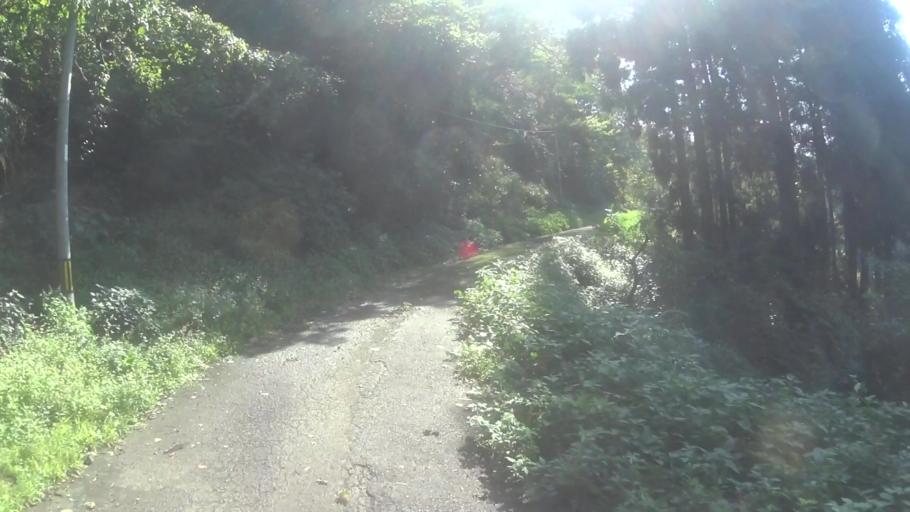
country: JP
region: Kyoto
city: Miyazu
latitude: 35.7169
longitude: 135.1658
